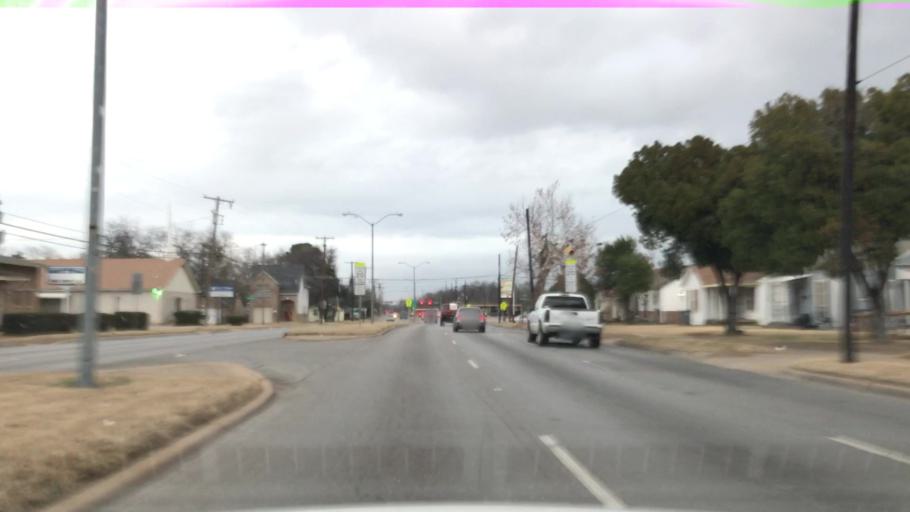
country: US
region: Texas
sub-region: Dallas County
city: Dallas
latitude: 32.7598
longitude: -96.7484
